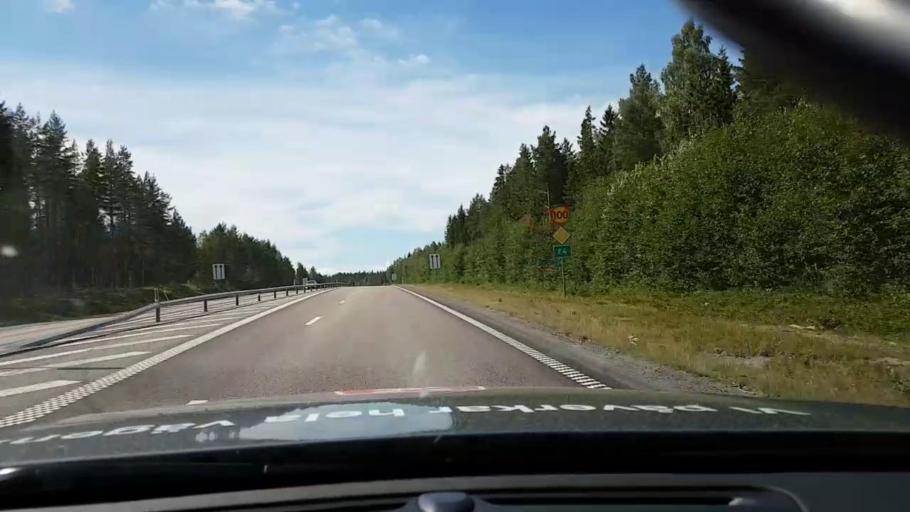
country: SE
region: Vaesternorrland
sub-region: OErnskoeldsviks Kommun
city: Husum
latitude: 63.3392
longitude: 19.0962
